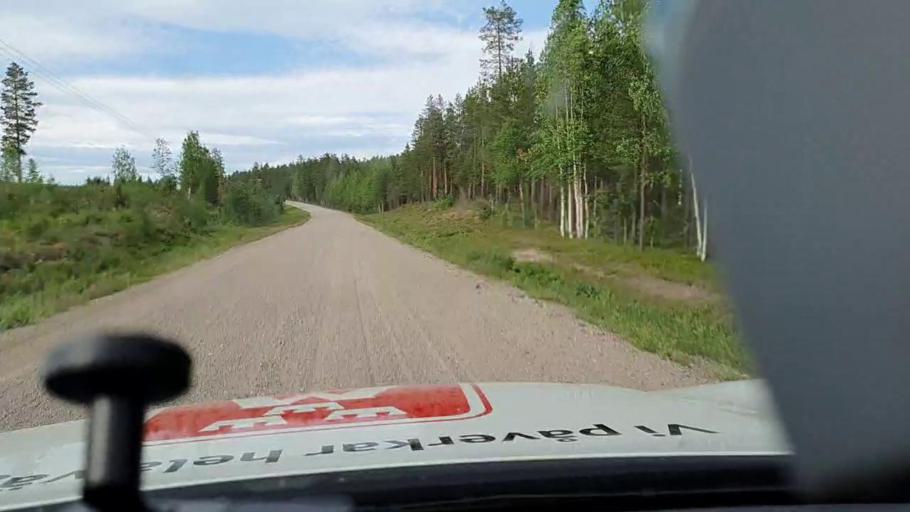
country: SE
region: Norrbotten
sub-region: Alvsbyns Kommun
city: AElvsbyn
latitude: 66.1277
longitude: 20.9975
